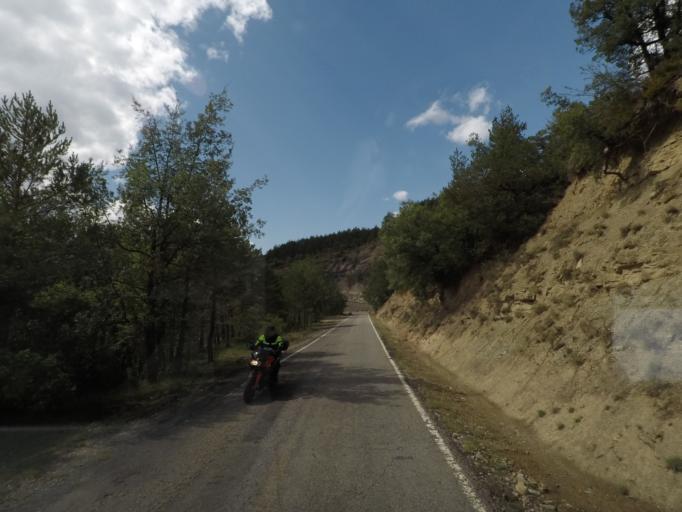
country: ES
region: Aragon
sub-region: Provincia de Huesca
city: Yebra de Basa
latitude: 42.4032
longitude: -0.2454
